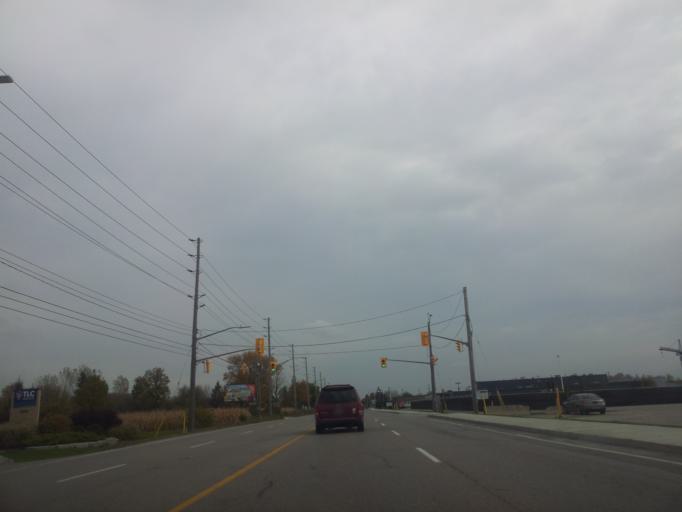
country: CA
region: Ontario
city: London
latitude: 43.0189
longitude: -81.1717
